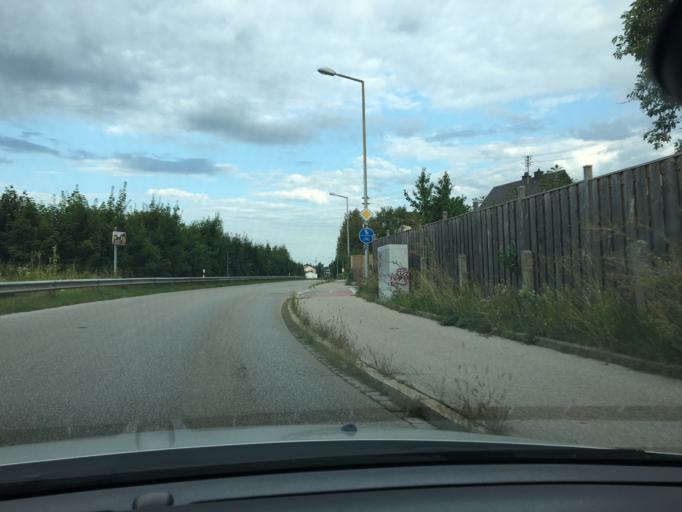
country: DE
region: Bavaria
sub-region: Upper Bavaria
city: Muehldorf
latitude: 48.2475
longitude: 12.5395
